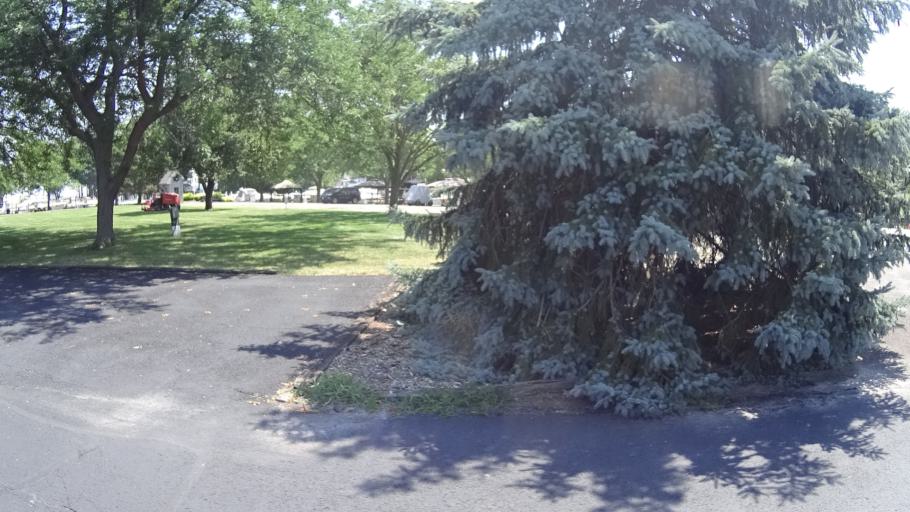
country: US
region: Ohio
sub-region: Erie County
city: Huron
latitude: 41.4120
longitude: -82.5935
